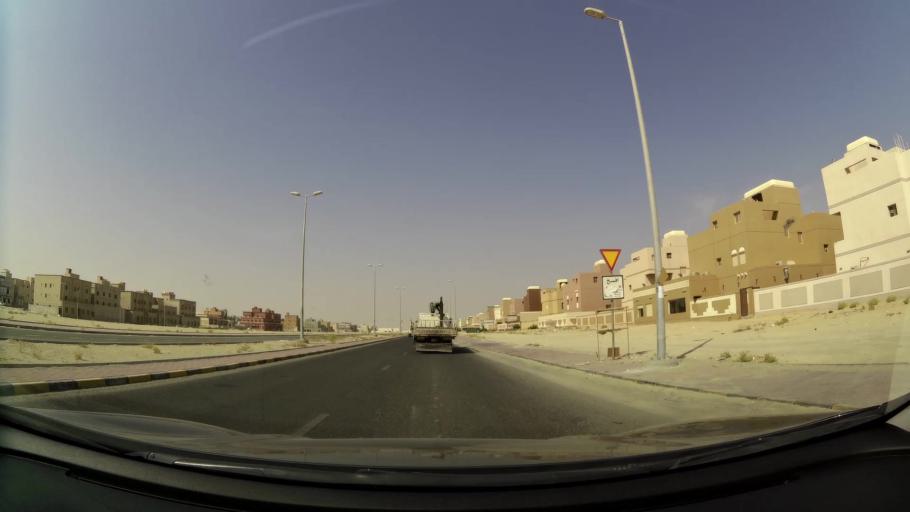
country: KW
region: Al Ahmadi
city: Al Wafrah
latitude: 28.7991
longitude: 48.0572
